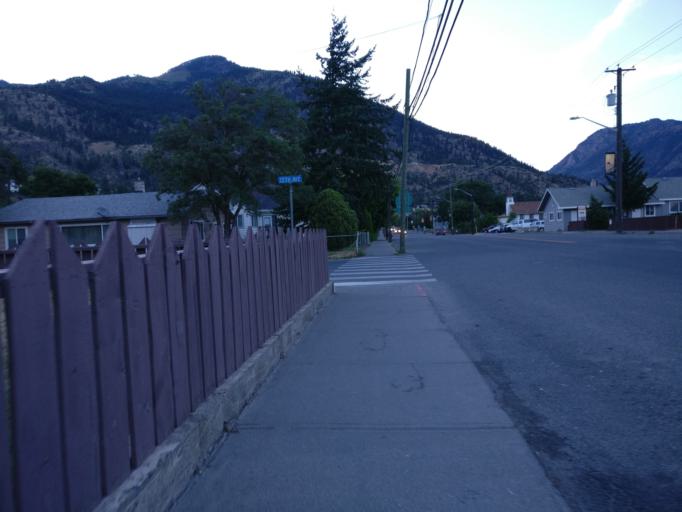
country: CA
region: British Columbia
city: Lillooet
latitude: 50.6867
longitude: -121.9369
